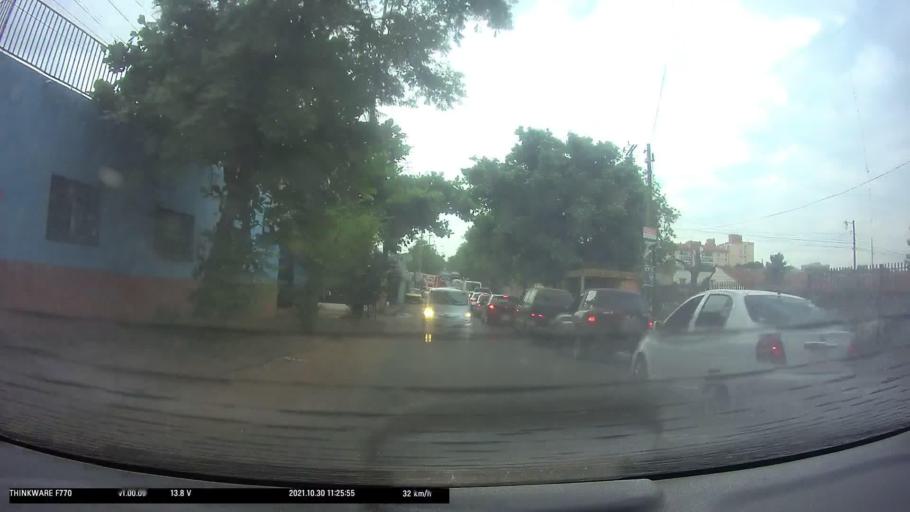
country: PY
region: Central
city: Fernando de la Mora
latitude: -25.3224
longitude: -57.5253
